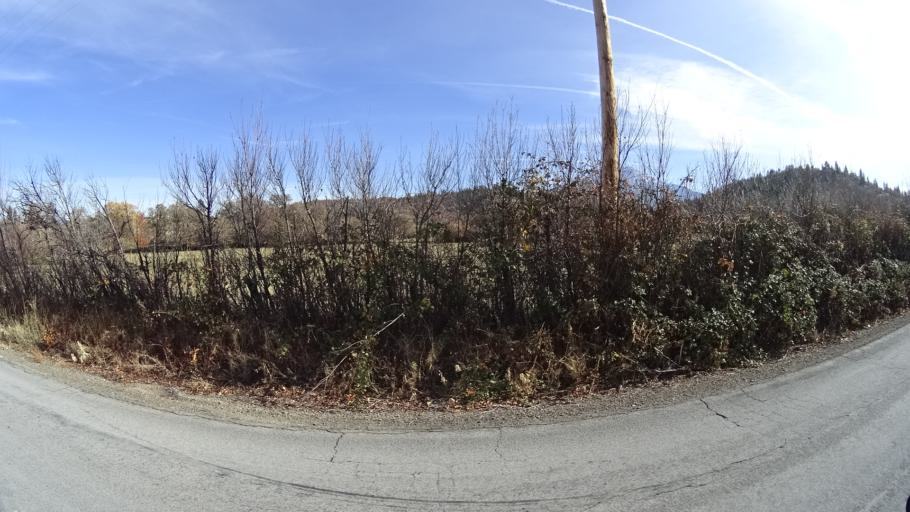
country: US
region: California
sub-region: Siskiyou County
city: Weed
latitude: 41.4541
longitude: -122.4313
